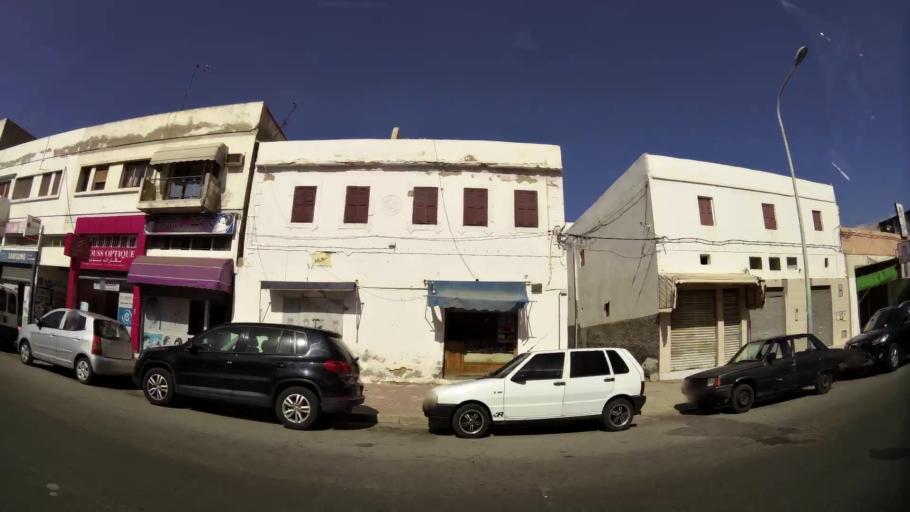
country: MA
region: Souss-Massa-Draa
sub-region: Agadir-Ida-ou-Tnan
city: Agadir
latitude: 30.4157
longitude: -9.5888
